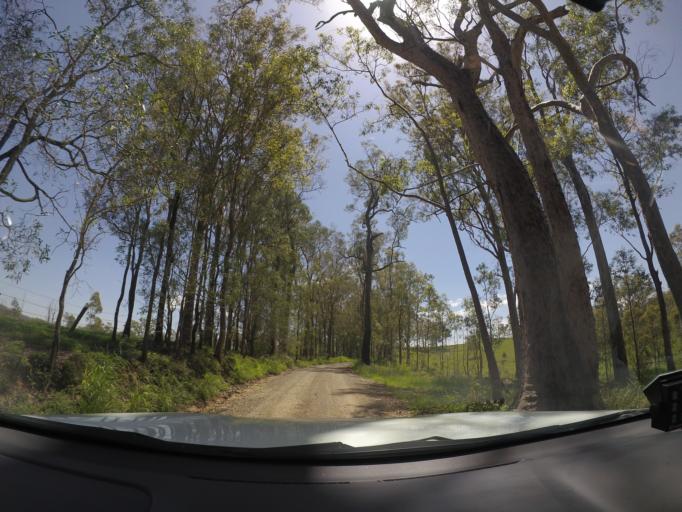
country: AU
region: Queensland
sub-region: Ipswich
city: Redbank Plains
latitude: -27.7876
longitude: 152.8410
